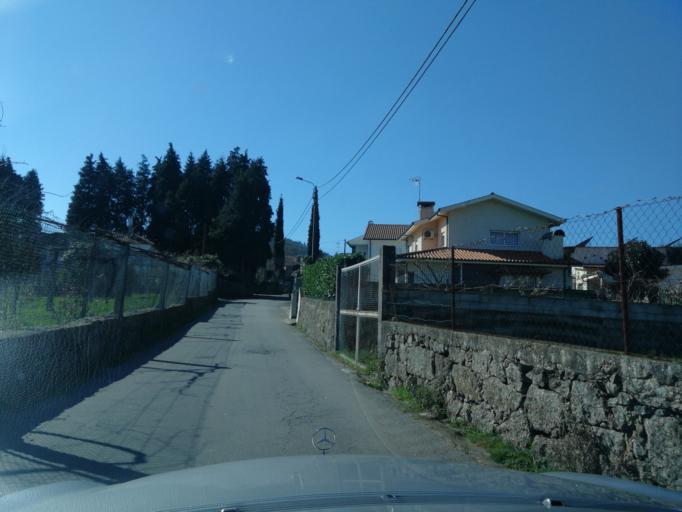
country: PT
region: Braga
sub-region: Vila Nova de Famalicao
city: Calendario
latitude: 41.3956
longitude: -8.5234
